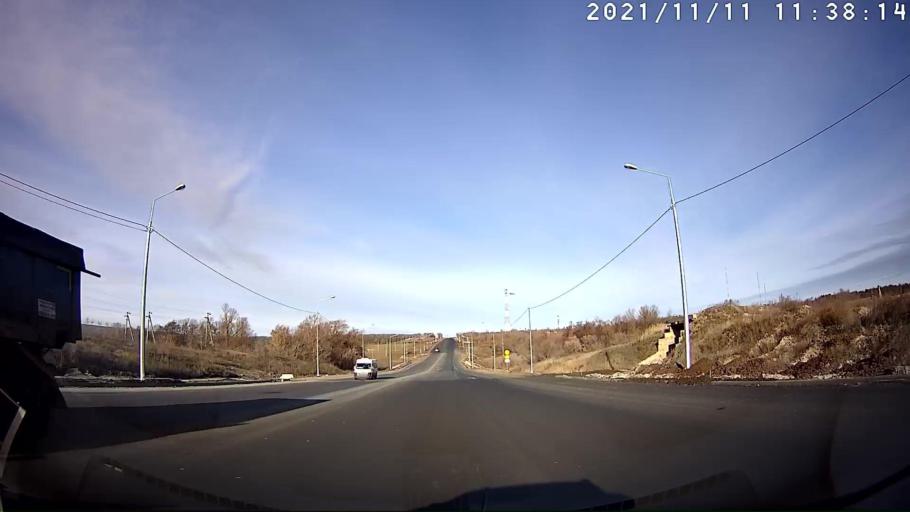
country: RU
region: Samara
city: Varlamovo
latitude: 53.3800
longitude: 48.3779
